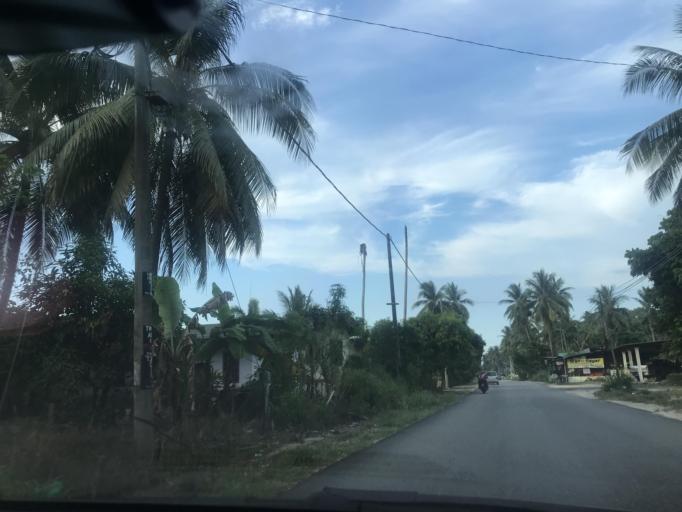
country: MY
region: Kelantan
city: Kota Bharu
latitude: 6.1270
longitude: 102.3576
